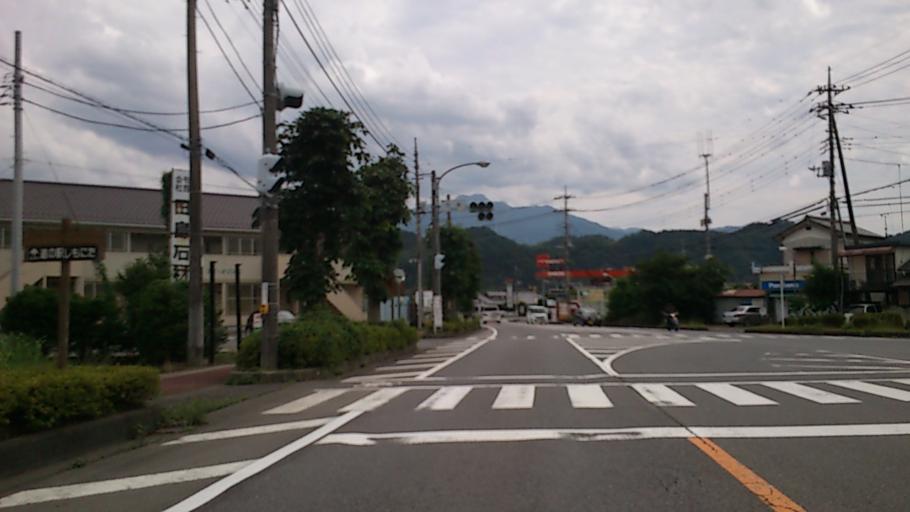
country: JP
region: Gunma
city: Tomioka
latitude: 36.2477
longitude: 138.8594
